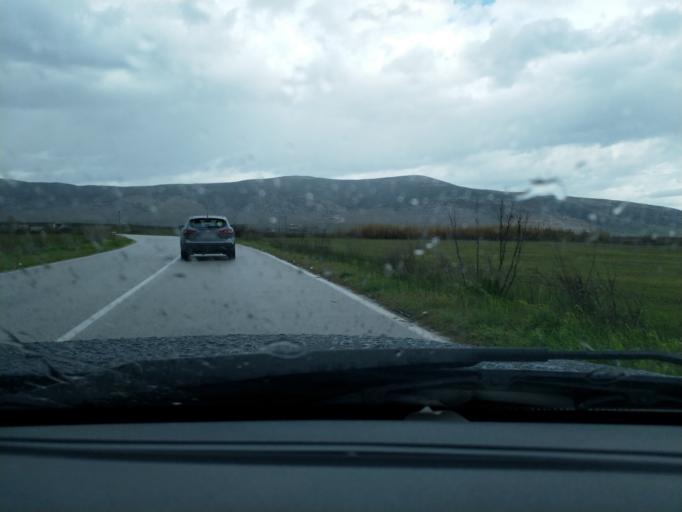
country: GR
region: Thessaly
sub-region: Trikala
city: Taxiarches
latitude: 39.5540
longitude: 21.8901
